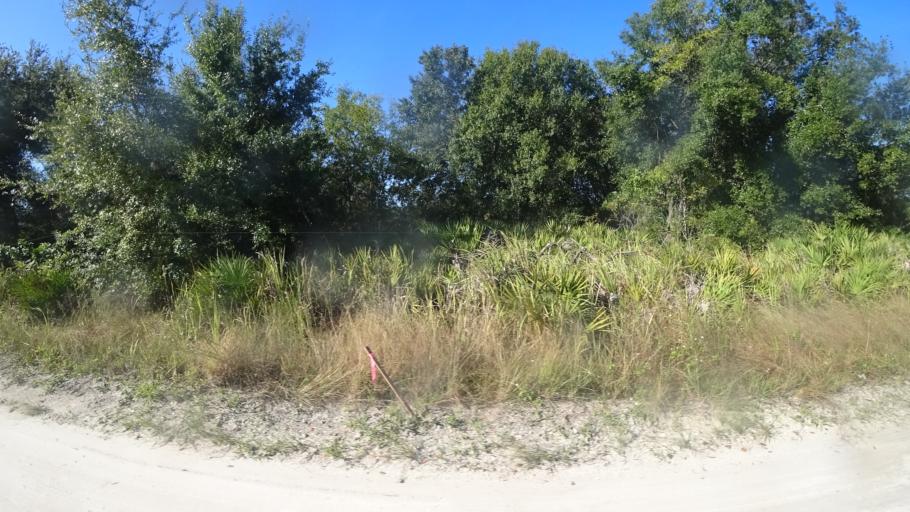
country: US
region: Florida
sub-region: Hillsborough County
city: Sun City Center
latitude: 27.6465
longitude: -82.3583
